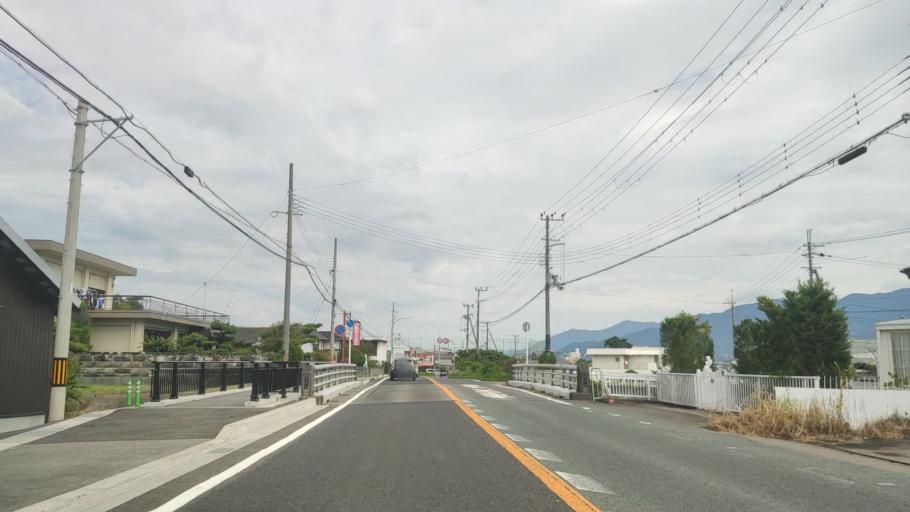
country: JP
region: Wakayama
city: Iwade
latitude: 34.2681
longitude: 135.3961
